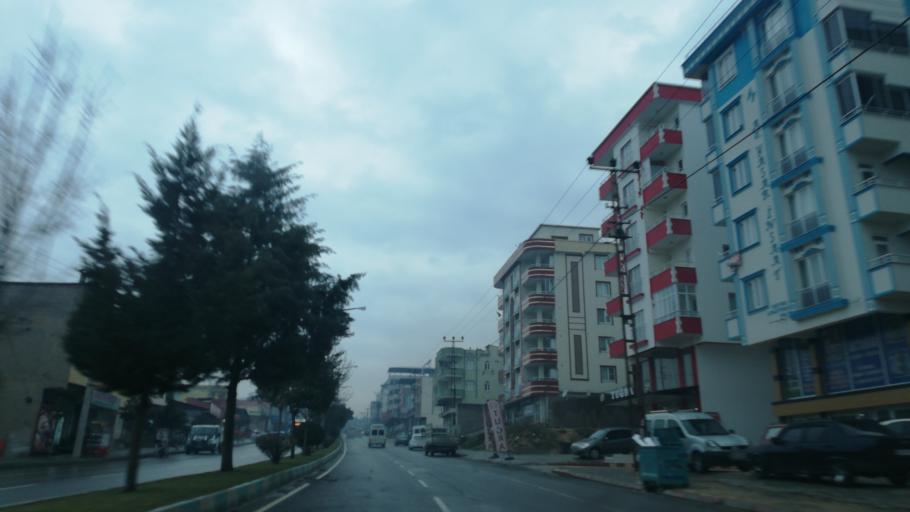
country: TR
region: Kahramanmaras
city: Kahramanmaras
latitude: 37.5822
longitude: 36.9554
